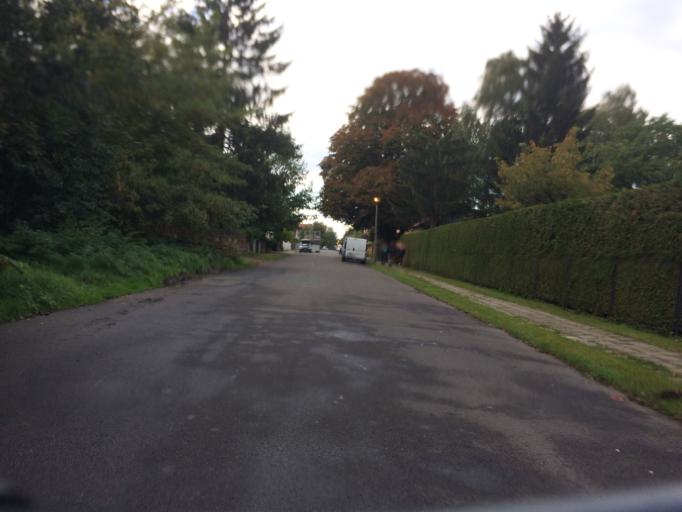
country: DE
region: Berlin
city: Karow
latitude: 52.6069
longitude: 13.4729
